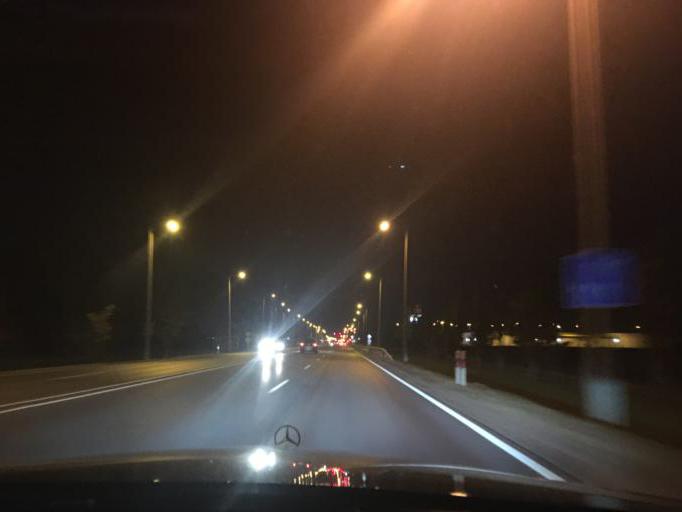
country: HU
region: Hajdu-Bihar
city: Debrecen
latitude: 47.4917
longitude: 21.6324
